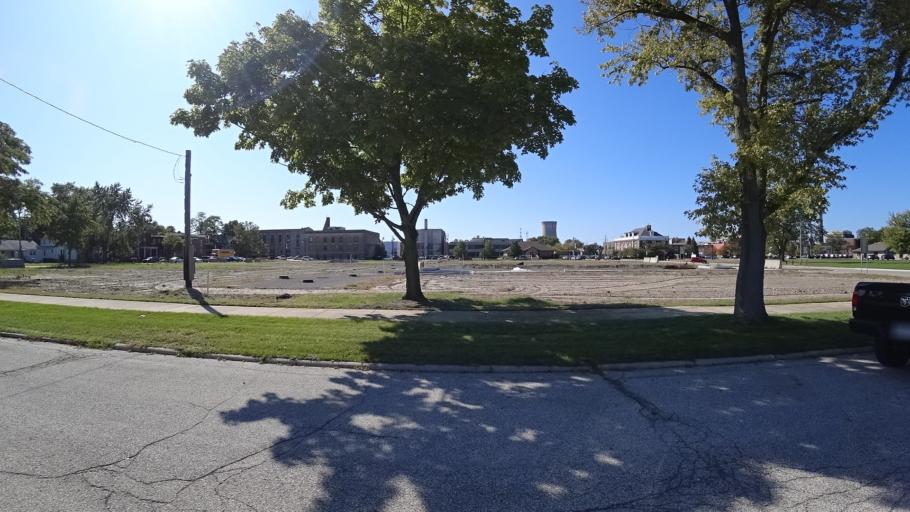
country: US
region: Indiana
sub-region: LaPorte County
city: Michigan City
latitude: 41.7176
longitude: -86.8987
